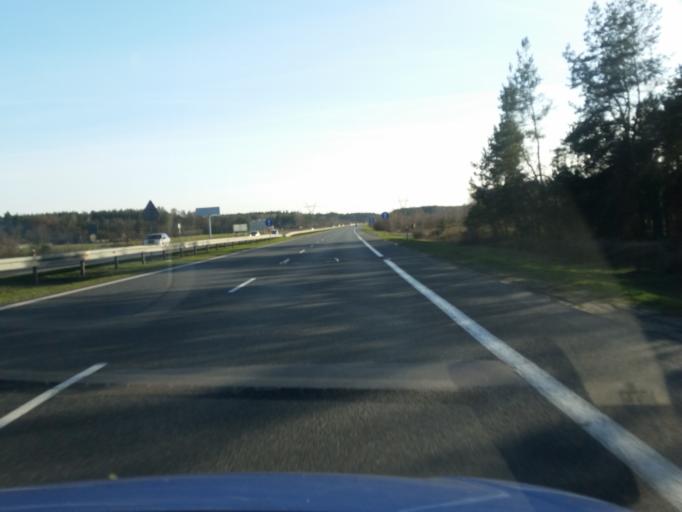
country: PL
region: Lodz Voivodeship
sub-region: Powiat radomszczanski
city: Radomsko
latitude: 51.0552
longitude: 19.3573
